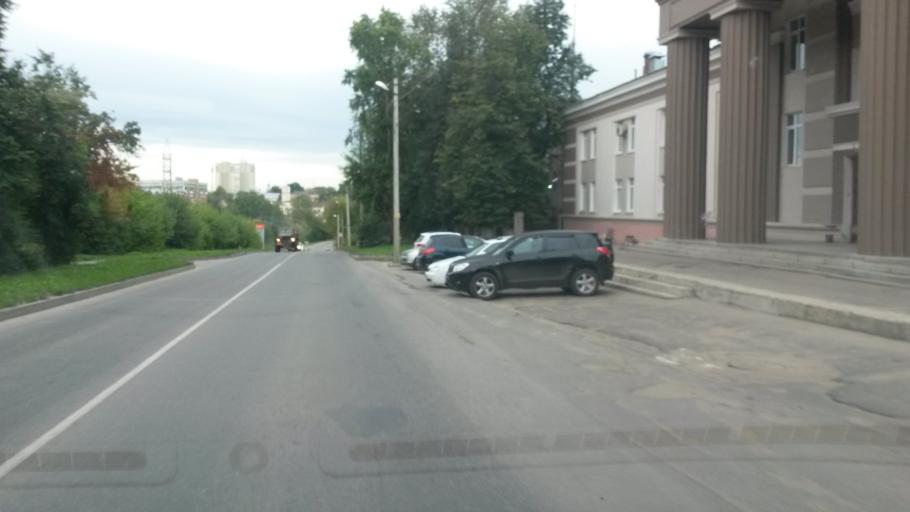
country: RU
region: Ivanovo
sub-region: Gorod Ivanovo
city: Ivanovo
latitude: 57.0166
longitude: 40.9568
